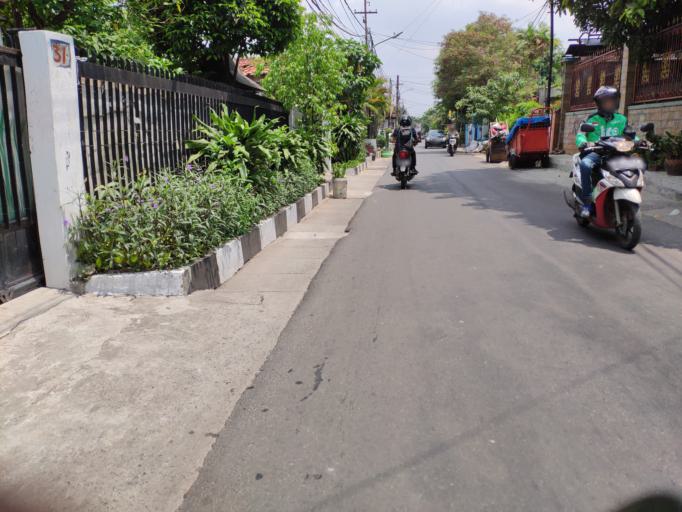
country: ID
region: Jakarta Raya
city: Jakarta
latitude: -6.2091
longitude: 106.8639
